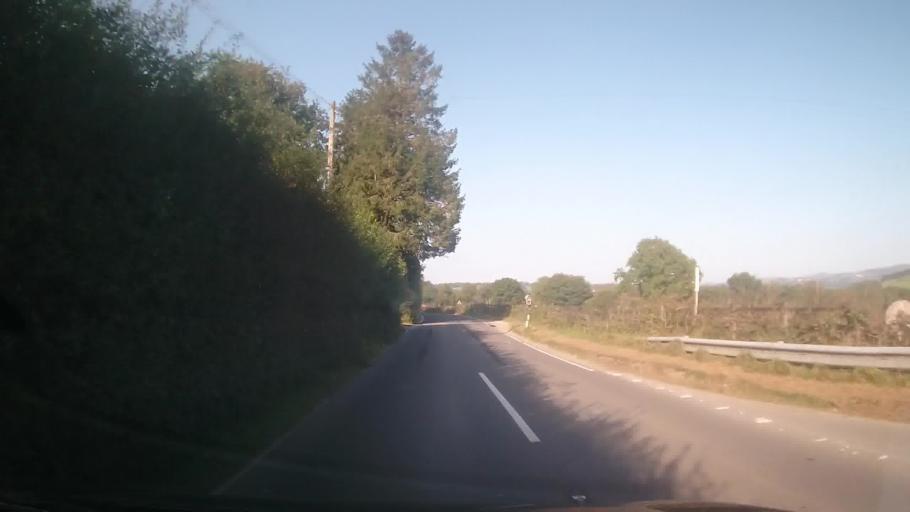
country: GB
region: Wales
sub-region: County of Ceredigion
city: Llangybi
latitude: 52.1807
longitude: -4.0022
